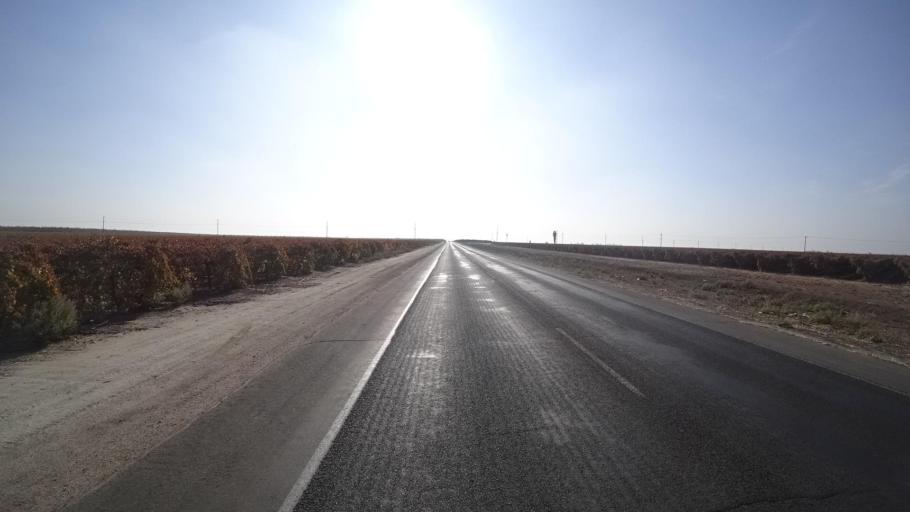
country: US
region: California
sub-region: Kern County
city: McFarland
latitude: 35.7064
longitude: -119.1668
